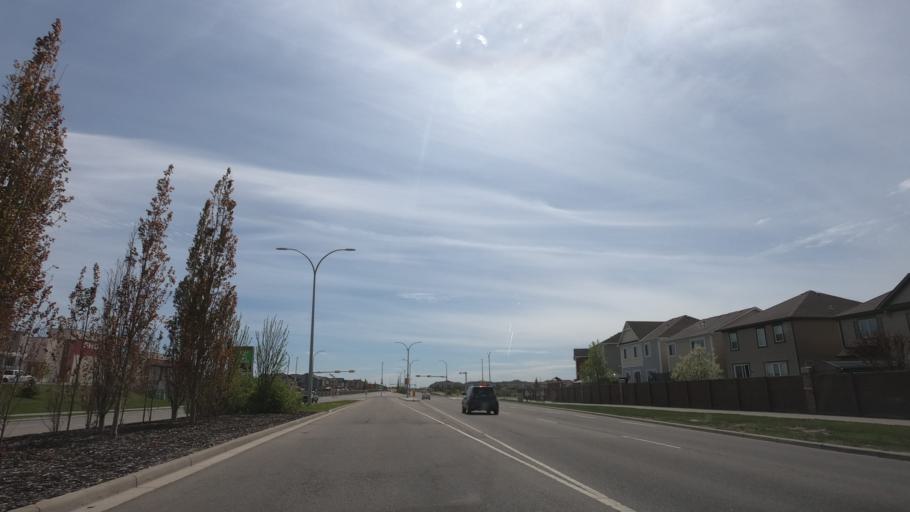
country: CA
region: Alberta
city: Airdrie
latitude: 51.2575
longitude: -114.0250
